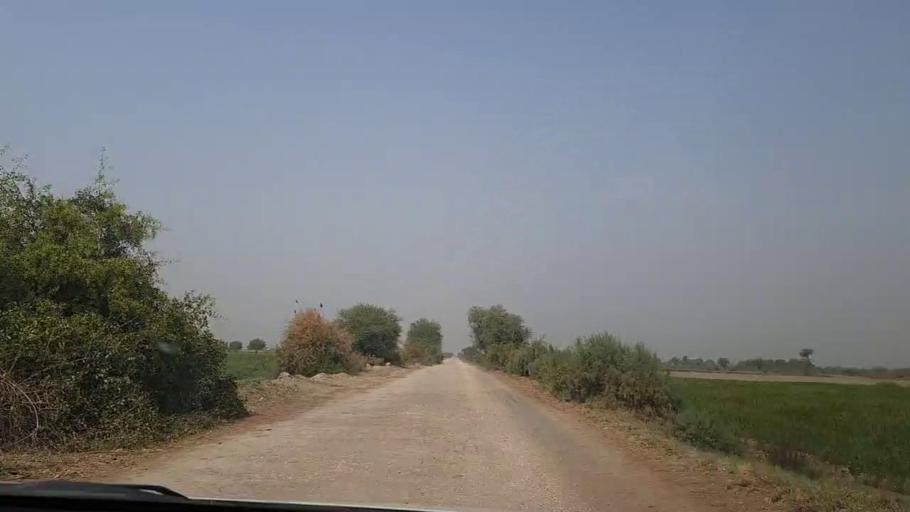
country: PK
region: Sindh
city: Mirpur Khas
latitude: 25.5872
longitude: 69.2010
